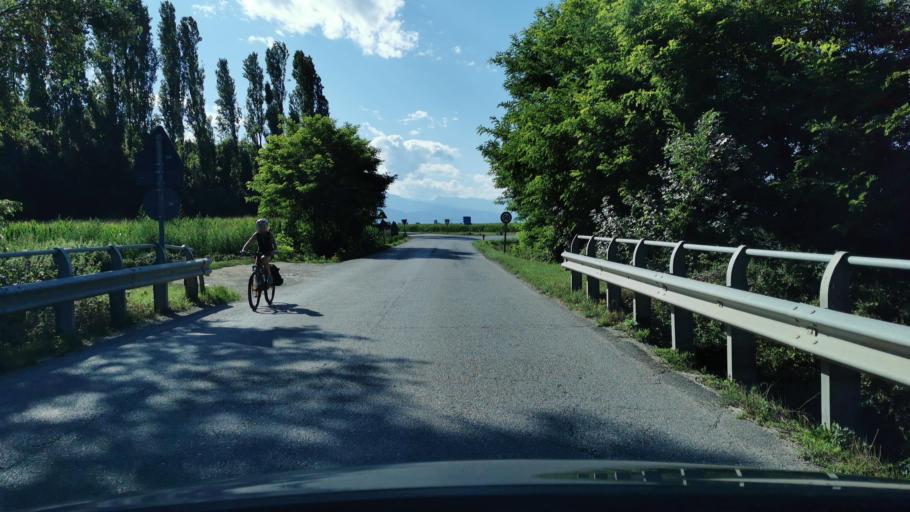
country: IT
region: Piedmont
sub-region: Provincia di Cuneo
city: Genola
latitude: 44.6100
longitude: 7.6229
